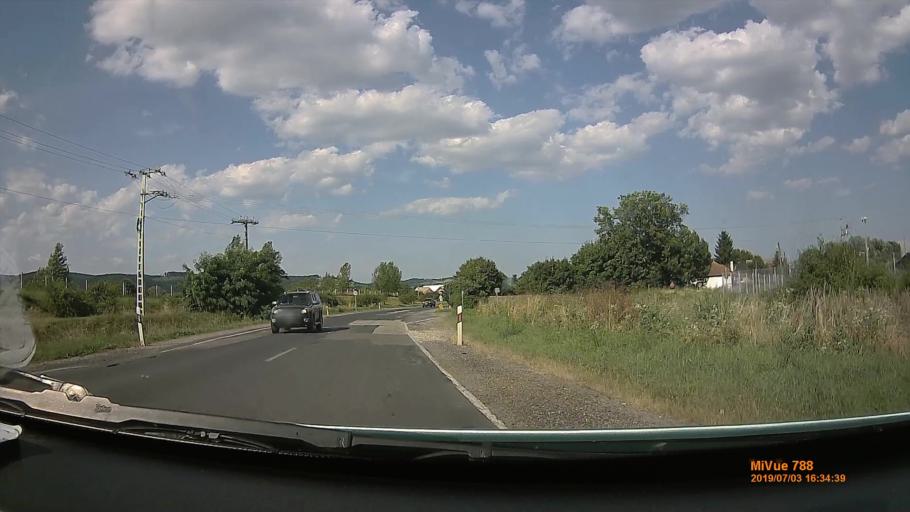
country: HU
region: Borsod-Abauj-Zemplen
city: Sajokaza
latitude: 48.2724
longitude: 20.5482
